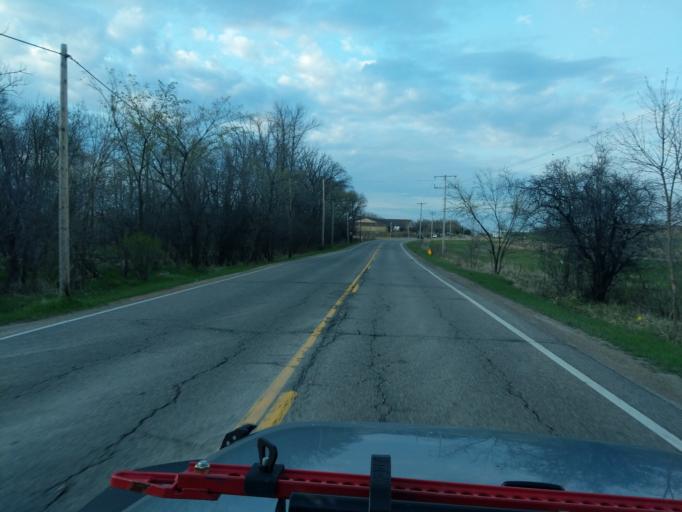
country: US
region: Minnesota
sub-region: Hennepin County
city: Rogers
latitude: 45.1792
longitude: -93.5222
